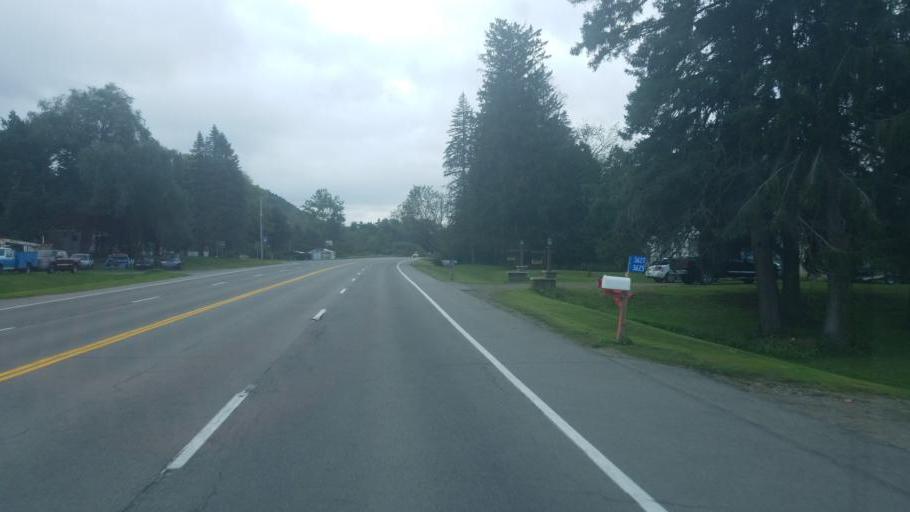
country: US
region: New York
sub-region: Cattaraugus County
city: Weston Mills
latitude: 42.1570
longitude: -78.3973
